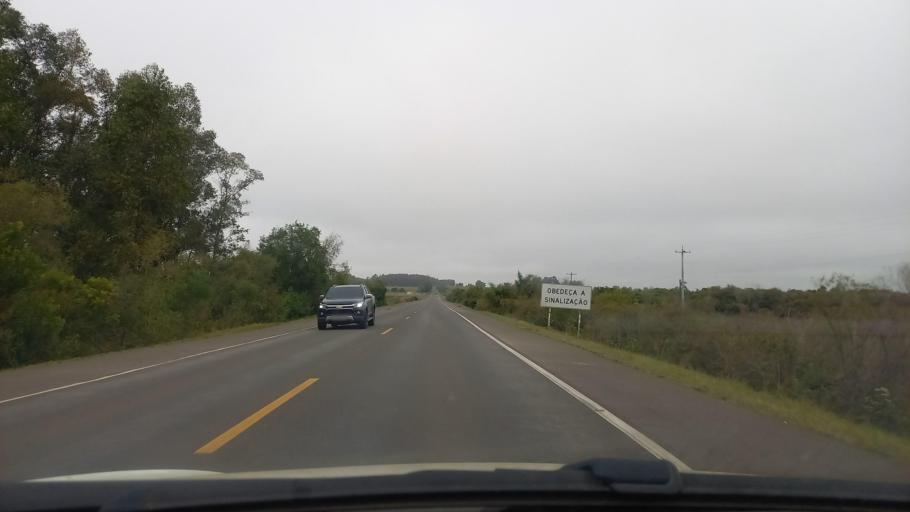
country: BR
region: Rio Grande do Sul
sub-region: Rosario Do Sul
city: Rosario do Sul
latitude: -30.3119
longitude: -54.9967
